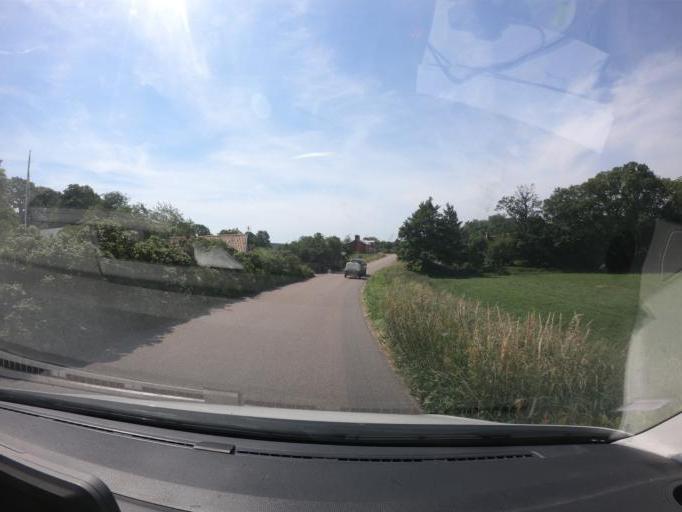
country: SE
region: Skane
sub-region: Angelholms Kommun
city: Vejbystrand
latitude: 56.4508
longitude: 12.7032
